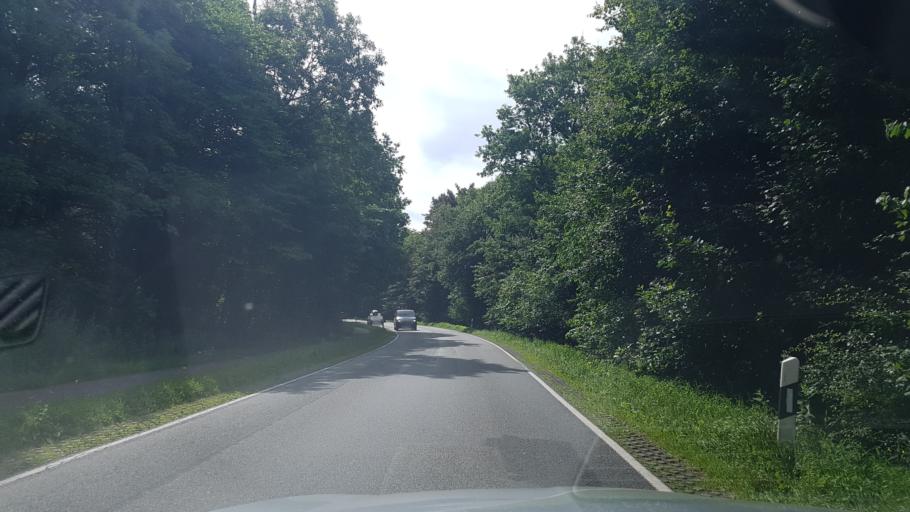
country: DE
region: Schleswig-Holstein
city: Handewitt
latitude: 54.7917
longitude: 9.3137
